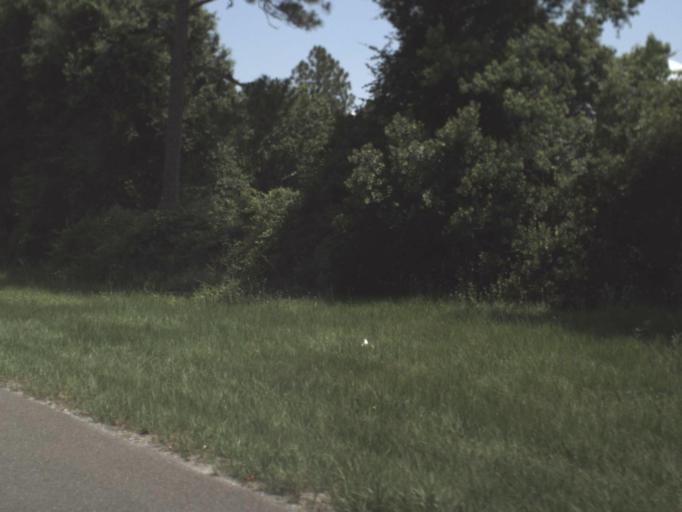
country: US
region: Florida
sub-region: Bradford County
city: Starke
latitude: 29.8954
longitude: -82.0867
